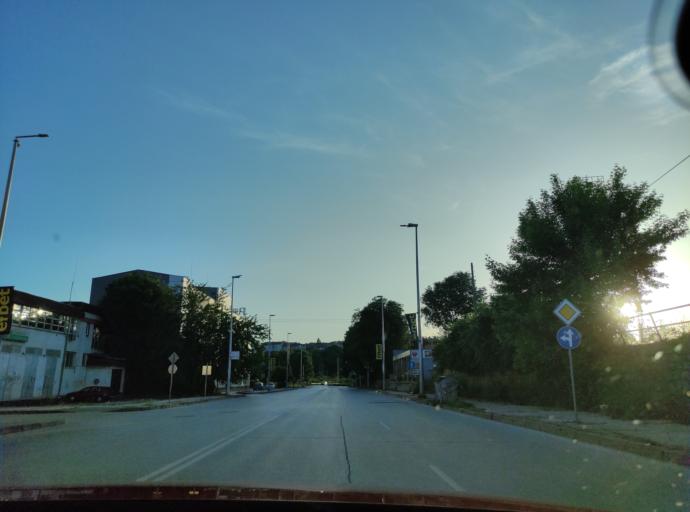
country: BG
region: Pleven
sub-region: Obshtina Pleven
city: Pleven
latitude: 43.4202
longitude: 24.6123
